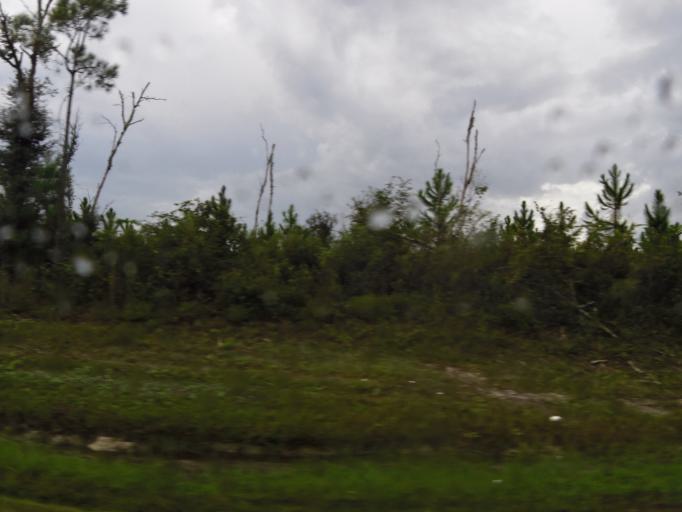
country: US
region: Florida
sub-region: Duval County
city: Baldwin
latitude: 30.4800
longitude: -81.9982
